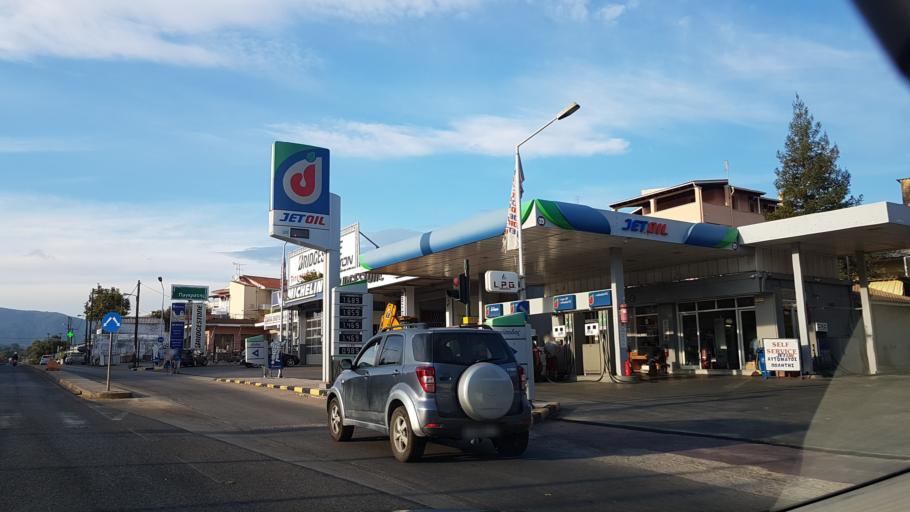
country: GR
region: Ionian Islands
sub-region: Nomos Kerkyras
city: Kontokali
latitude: 39.6547
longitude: 19.8407
